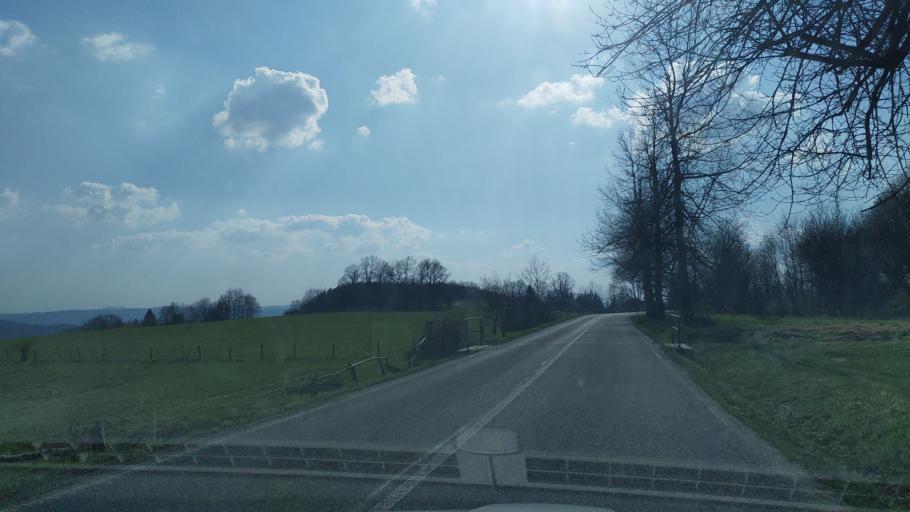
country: CZ
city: Kamenicky Senov
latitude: 50.7662
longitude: 14.4584
